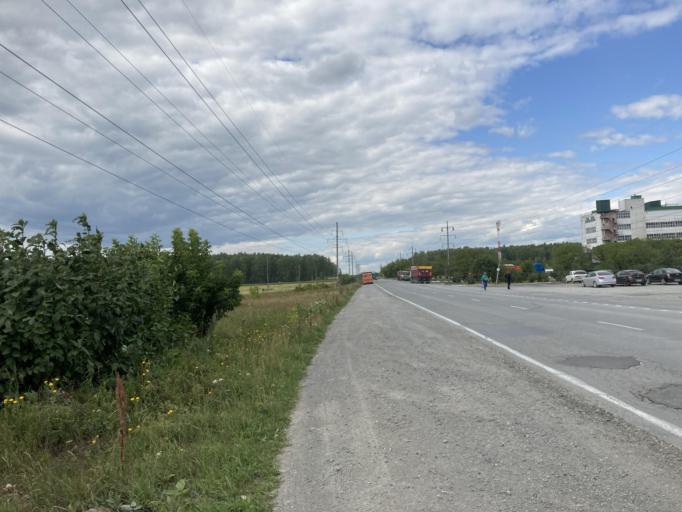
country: RU
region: Sverdlovsk
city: Bogdanovich
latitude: 56.8041
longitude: 62.0357
